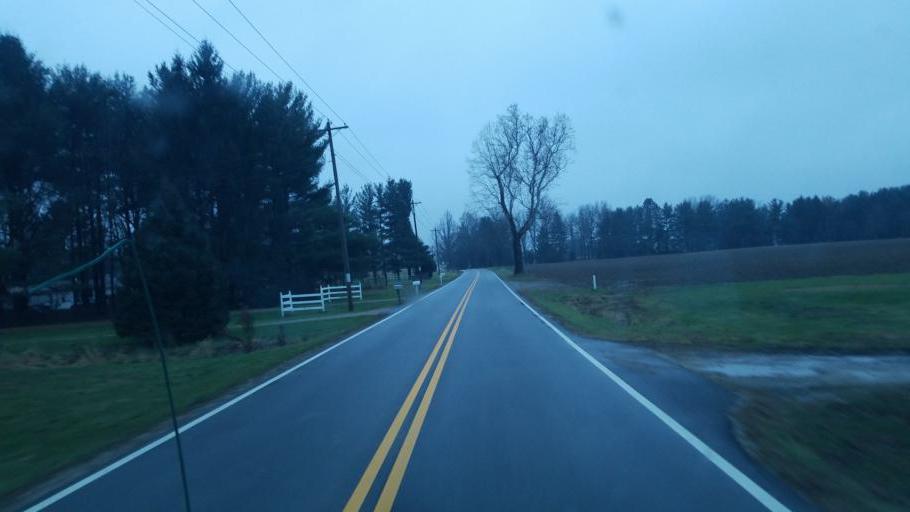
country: US
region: Ohio
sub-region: Delaware County
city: Ashley
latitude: 40.3378
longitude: -82.9195
